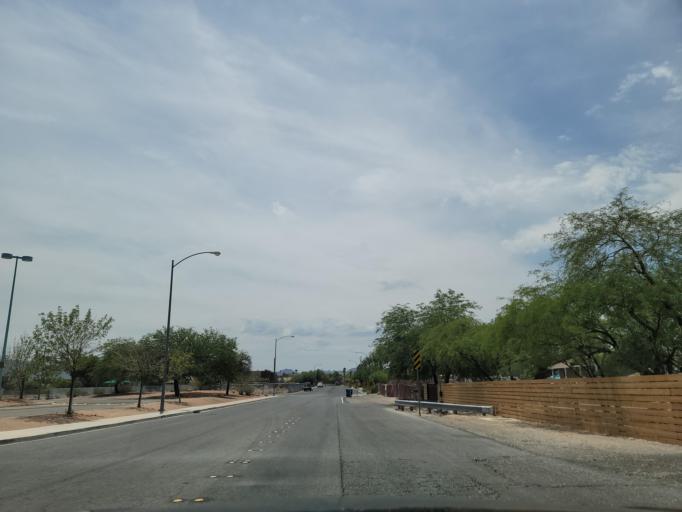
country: US
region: Nevada
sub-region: Clark County
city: Whitney
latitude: 36.0235
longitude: -115.1319
